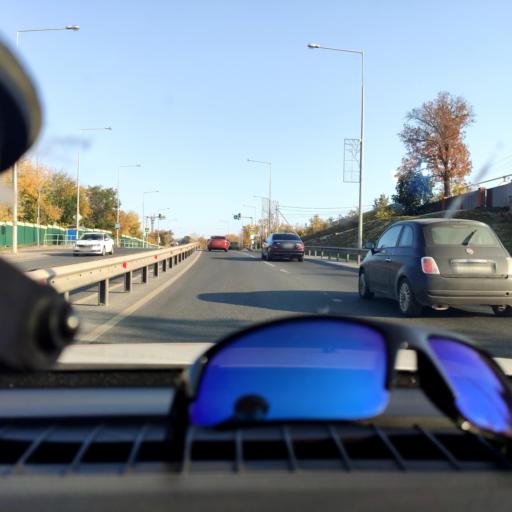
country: RU
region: Samara
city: Volzhskiy
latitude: 53.3661
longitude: 50.1956
